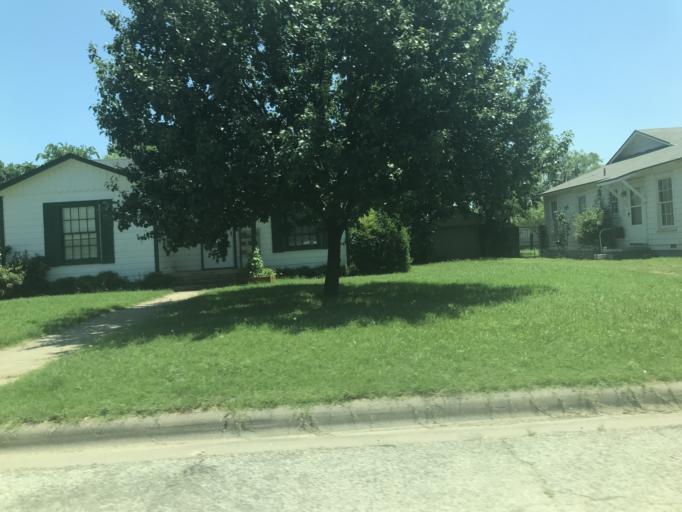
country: US
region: Texas
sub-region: Taylor County
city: Abilene
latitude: 32.4608
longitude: -99.7087
